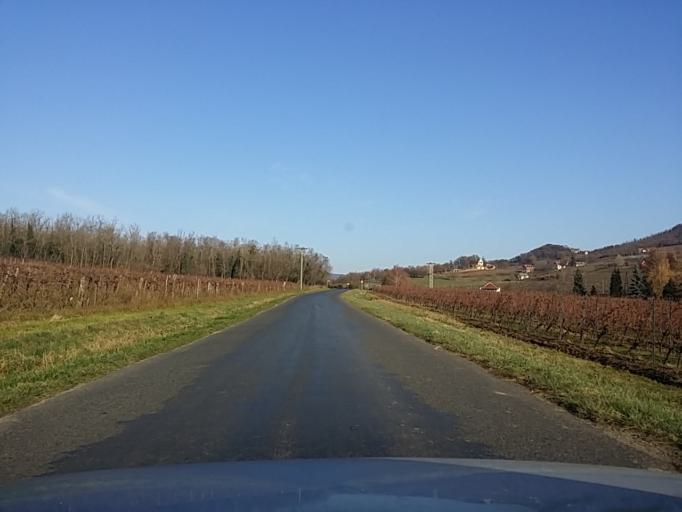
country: HU
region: Veszprem
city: Badacsonytomaj
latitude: 46.8270
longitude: 17.5140
